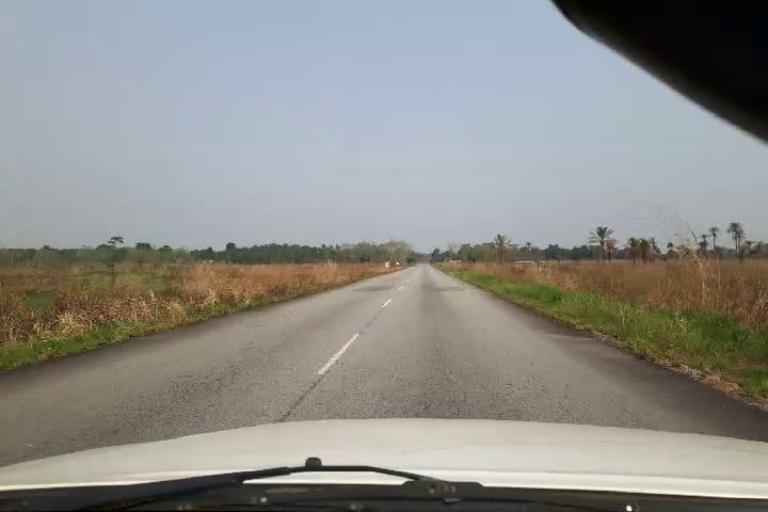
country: SL
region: Southern Province
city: Baiima
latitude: 8.1455
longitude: -11.9031
